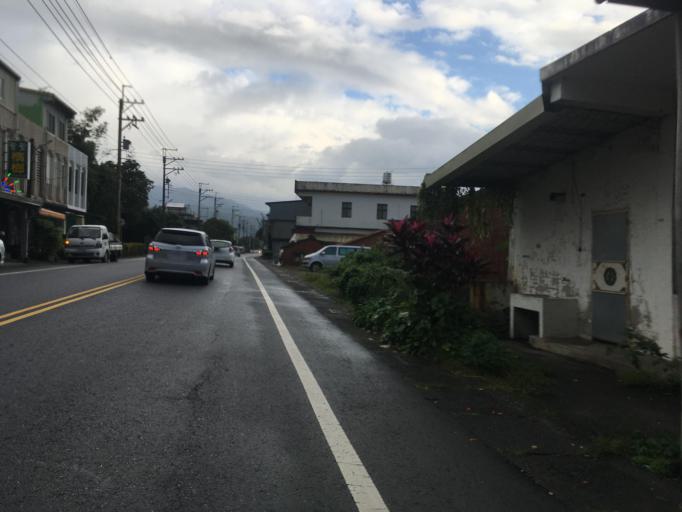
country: TW
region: Taiwan
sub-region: Yilan
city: Yilan
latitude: 24.8367
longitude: 121.8046
